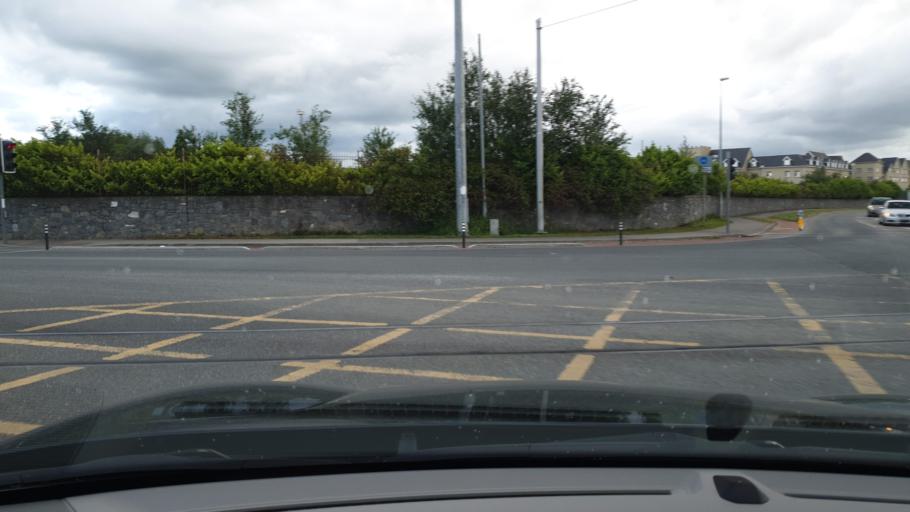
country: IE
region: Leinster
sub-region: South Dublin
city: Saggart
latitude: 53.2845
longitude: -6.4331
